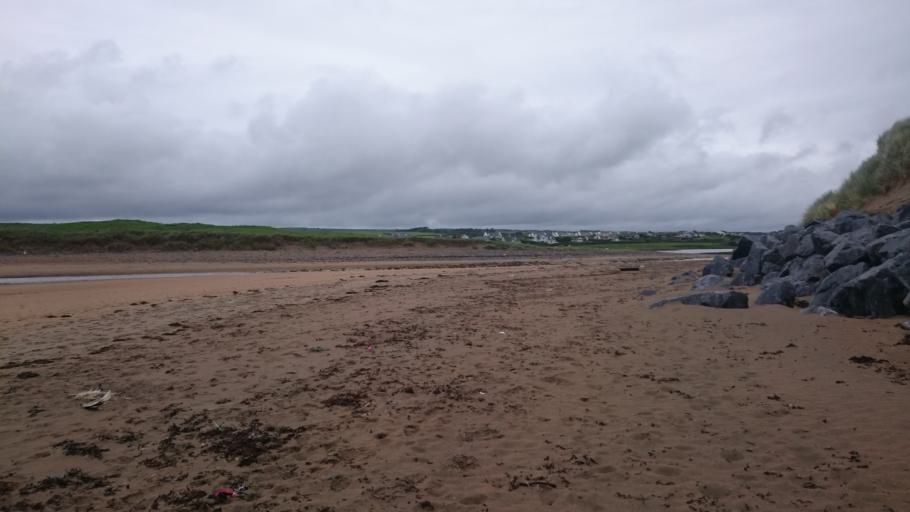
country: IE
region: Munster
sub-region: An Clar
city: Kilrush
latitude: 52.9425
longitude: -9.3585
